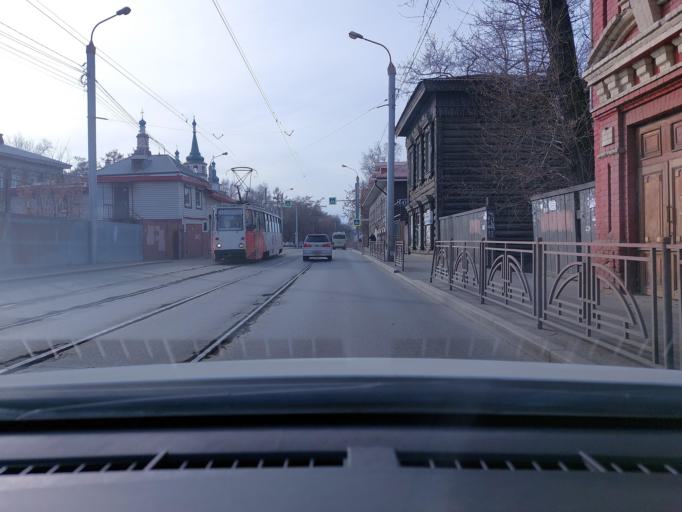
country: RU
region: Irkutsk
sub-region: Irkutskiy Rayon
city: Irkutsk
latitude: 52.2778
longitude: 104.2898
